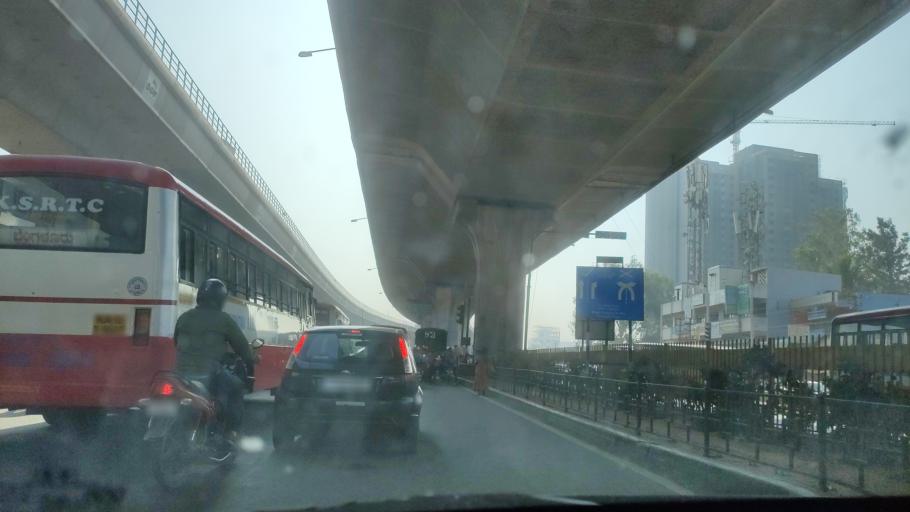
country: IN
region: Karnataka
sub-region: Bangalore Urban
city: Yelahanka
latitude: 13.0455
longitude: 77.5068
